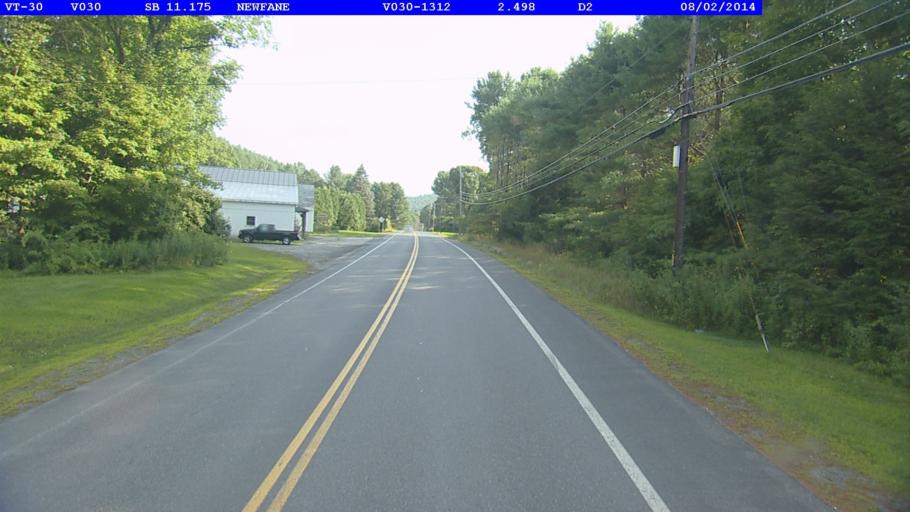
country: US
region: Vermont
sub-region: Windham County
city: Newfane
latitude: 42.9800
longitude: -72.6571
